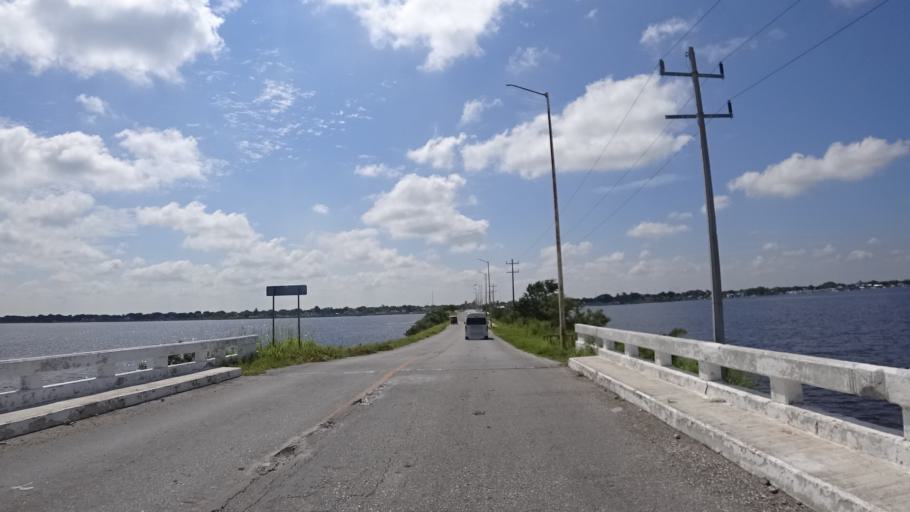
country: MX
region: Campeche
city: Sabancuy
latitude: 18.9814
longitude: -91.1839
